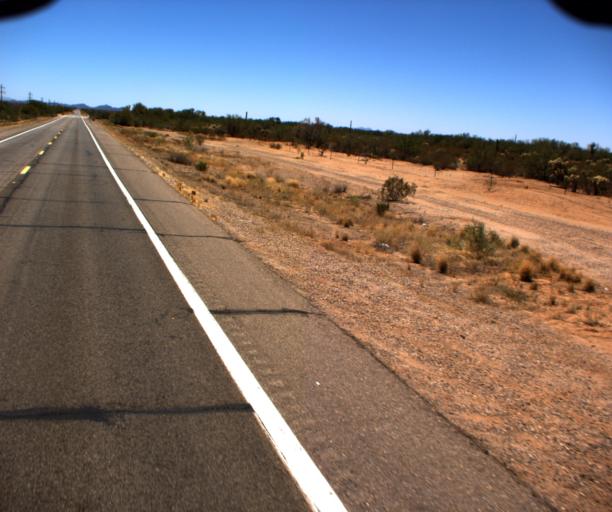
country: US
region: Arizona
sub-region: Pima County
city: Sells
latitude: 32.0925
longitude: -112.0595
